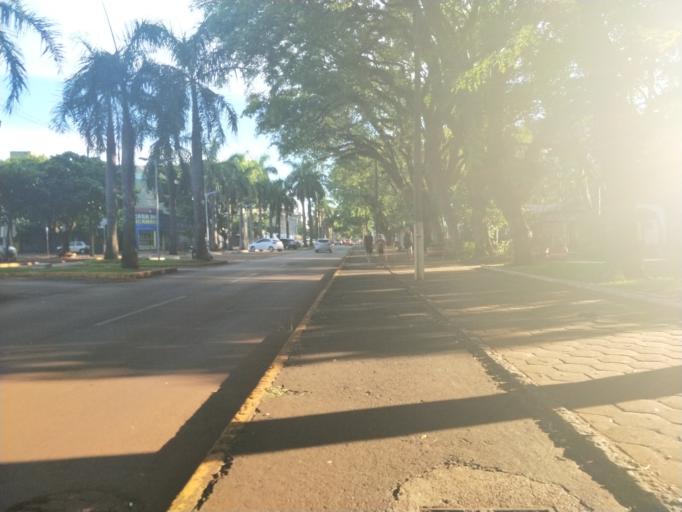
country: BR
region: Parana
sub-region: Marechal Candido Rondon
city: Marechal Candido Rondon
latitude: -24.5573
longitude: -54.0570
